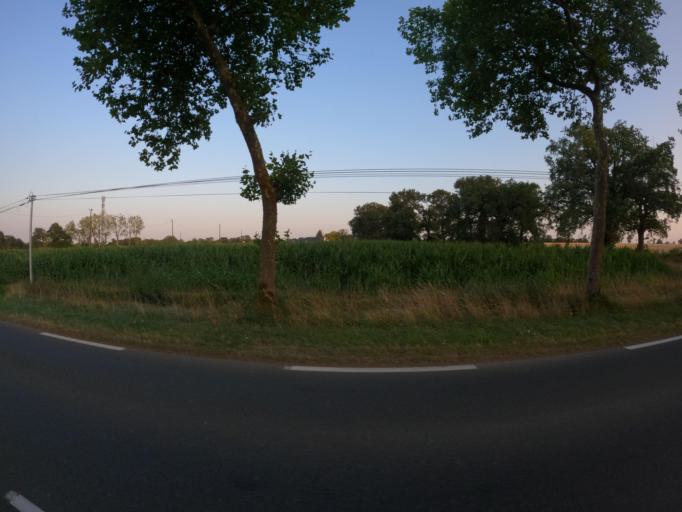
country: FR
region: Pays de la Loire
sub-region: Departement de la Mayenne
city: Meslay-du-Maine
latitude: 47.8715
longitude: -0.5347
